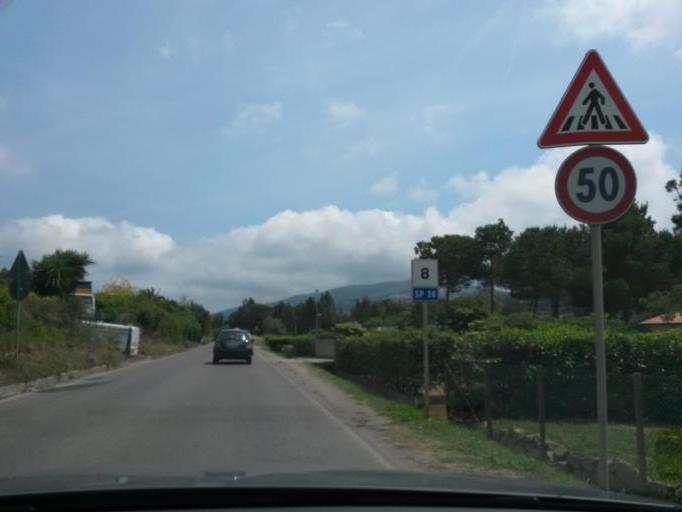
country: IT
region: Tuscany
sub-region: Provincia di Livorno
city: Capoliveri
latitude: 42.7632
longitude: 10.3602
